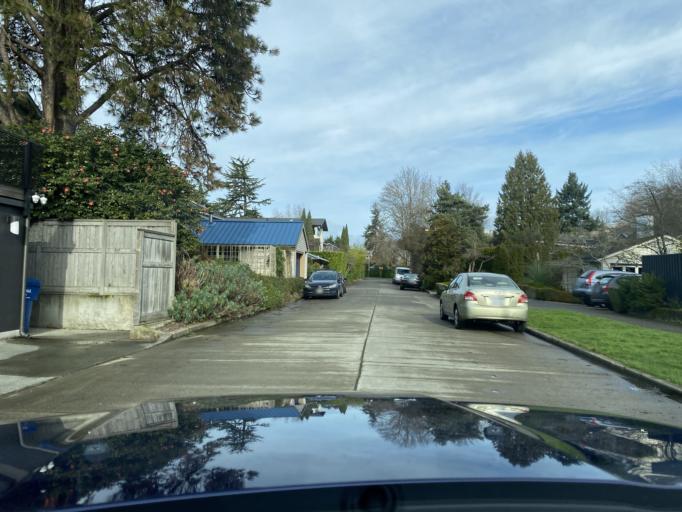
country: US
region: Washington
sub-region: King County
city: Medina
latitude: 47.6298
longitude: -122.2794
